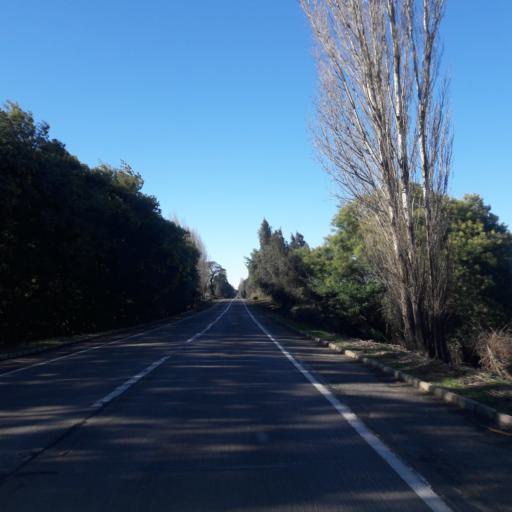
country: CL
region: Araucania
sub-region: Provincia de Malleco
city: Angol
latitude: -37.7549
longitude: -72.5805
